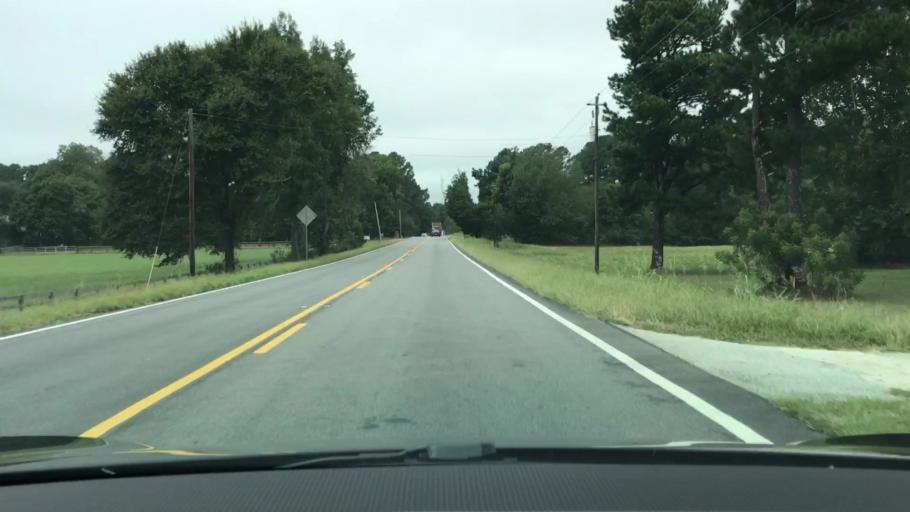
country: US
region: Georgia
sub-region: Greene County
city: Greensboro
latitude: 33.5671
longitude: -83.1584
